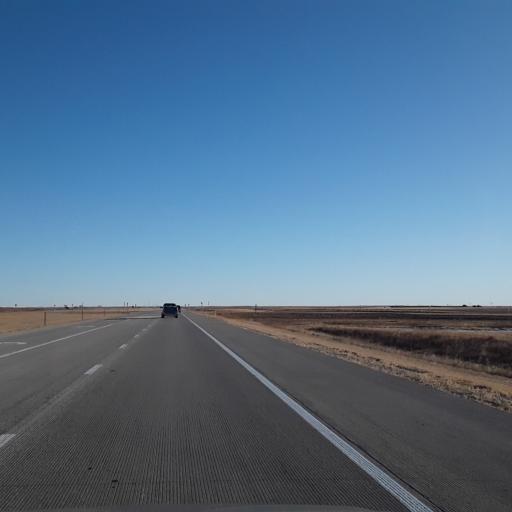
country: US
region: Kansas
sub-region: Seward County
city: Liberal
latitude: 37.1019
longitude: -100.7986
